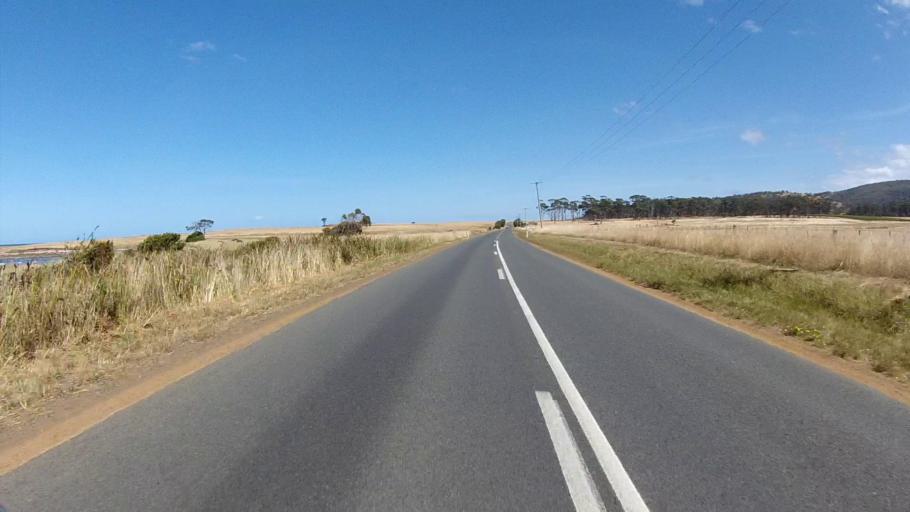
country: AU
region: Tasmania
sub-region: Sorell
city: Sorell
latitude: -42.2042
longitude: 148.0428
